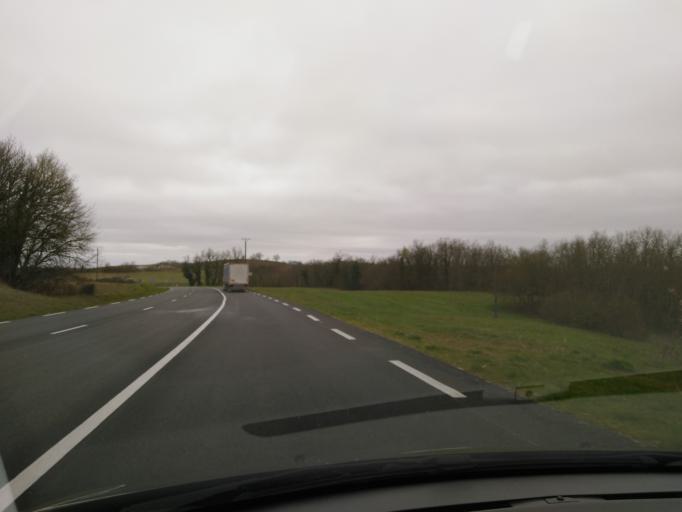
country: FR
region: Aquitaine
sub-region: Departement de la Dordogne
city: Monbazillac
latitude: 44.7288
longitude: 0.5488
